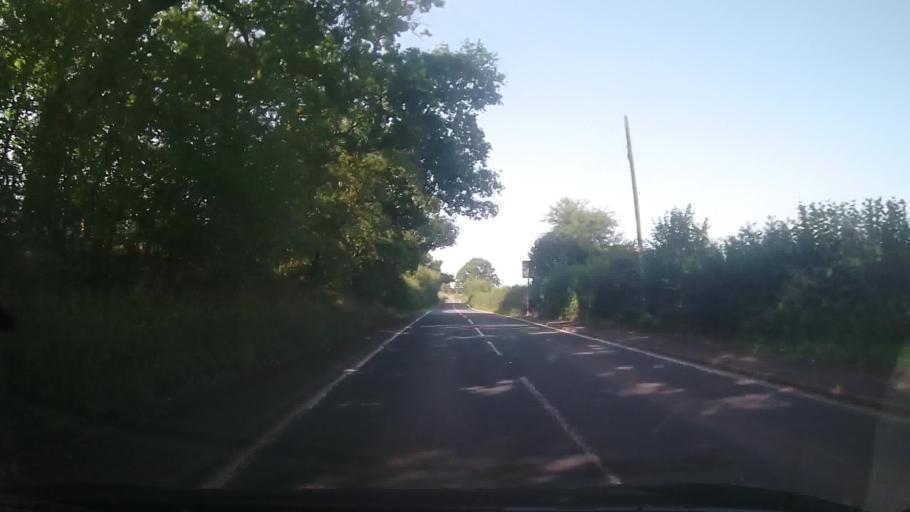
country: GB
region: Wales
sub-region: Sir Powys
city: Builth Wells
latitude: 52.1495
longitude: -3.4204
